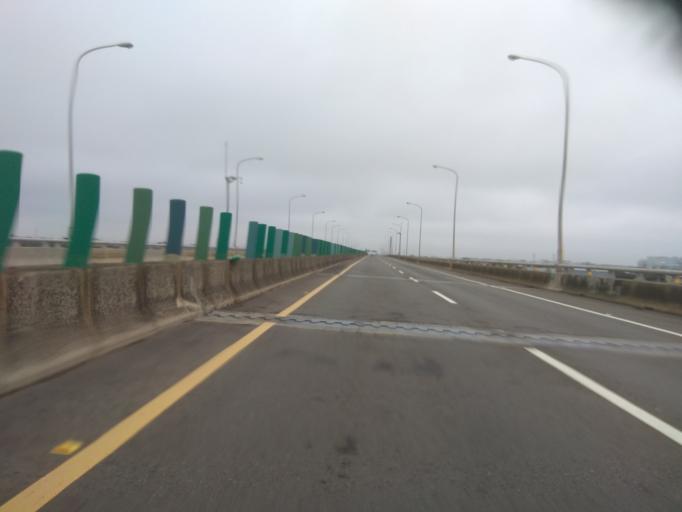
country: TW
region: Taiwan
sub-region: Hsinchu
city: Zhubei
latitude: 25.0019
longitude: 121.0982
